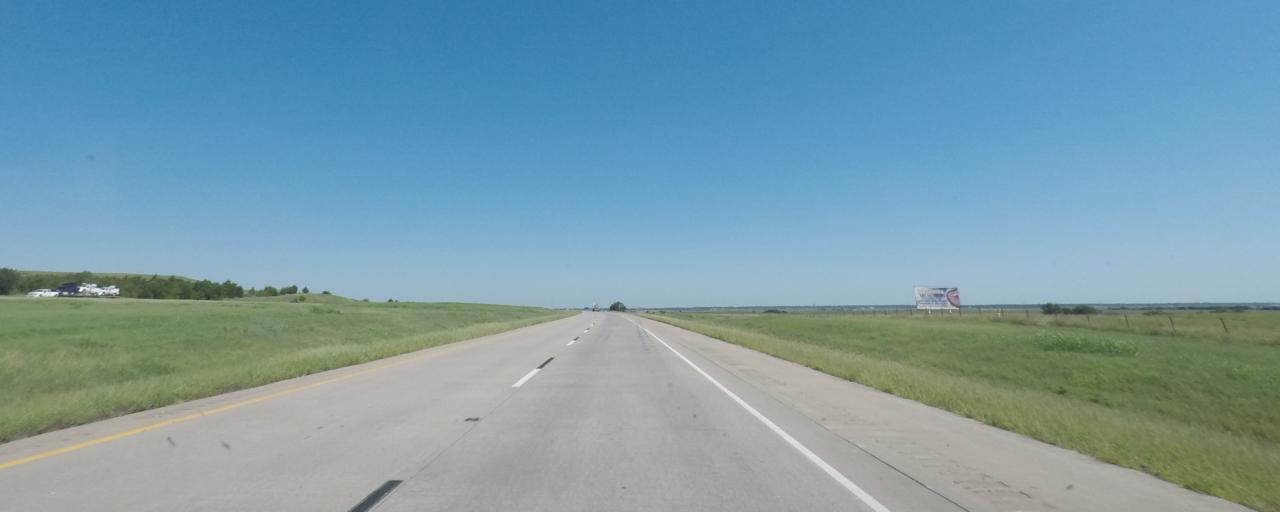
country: US
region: Oklahoma
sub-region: Kay County
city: Tonkawa
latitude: 36.5910
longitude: -97.3454
